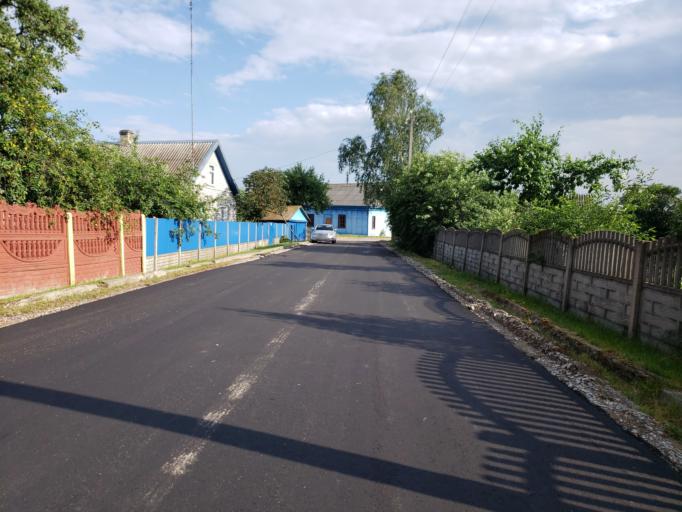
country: BY
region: Minsk
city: Chervyen'
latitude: 53.7156
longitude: 28.4041
